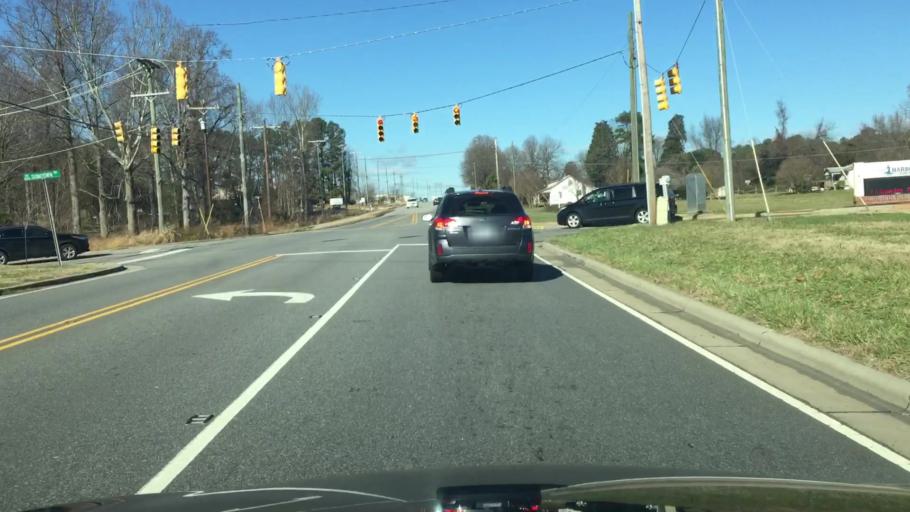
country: US
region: North Carolina
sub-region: Iredell County
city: Mooresville
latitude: 35.5778
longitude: -80.8711
